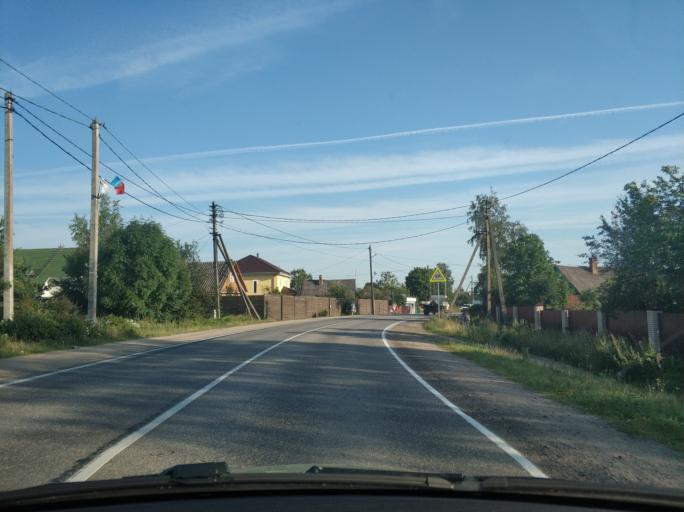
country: RU
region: Leningrad
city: Borisova Griva
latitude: 60.0899
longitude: 31.0187
